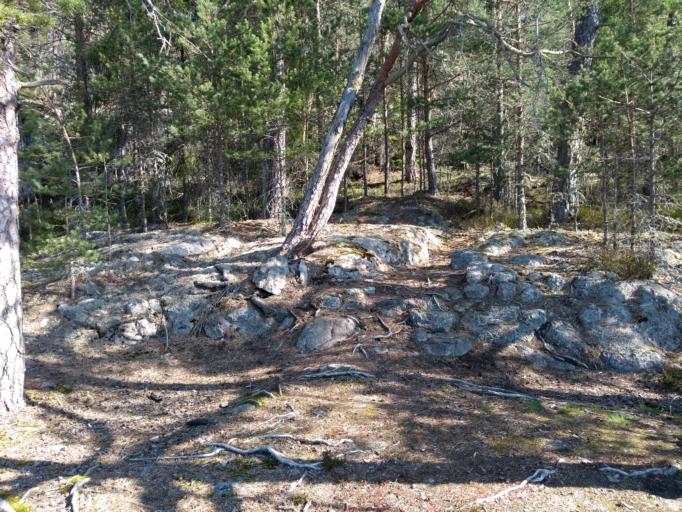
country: SE
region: OEstergoetland
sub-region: Norrkopings Kommun
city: Krokek
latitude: 58.6483
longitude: 16.5329
